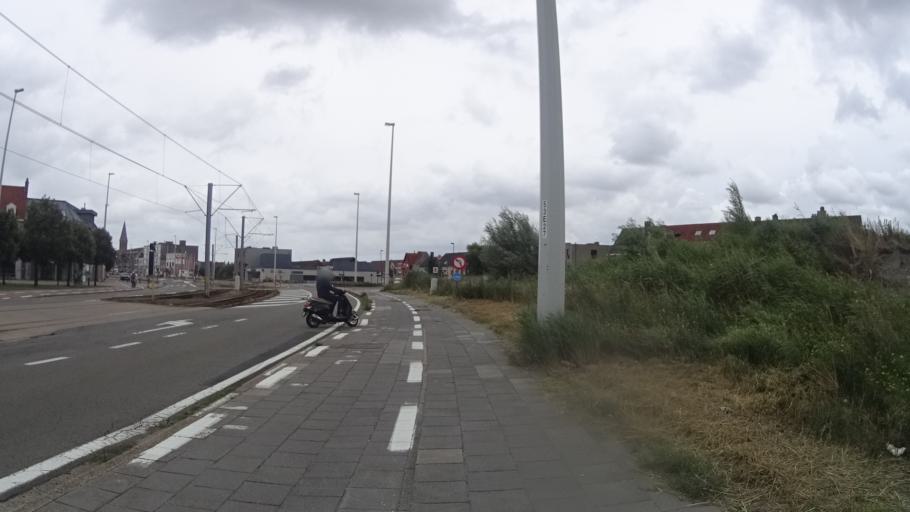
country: BE
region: Flanders
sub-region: Provincie West-Vlaanderen
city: Zeebrugge
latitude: 51.3291
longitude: 3.2029
